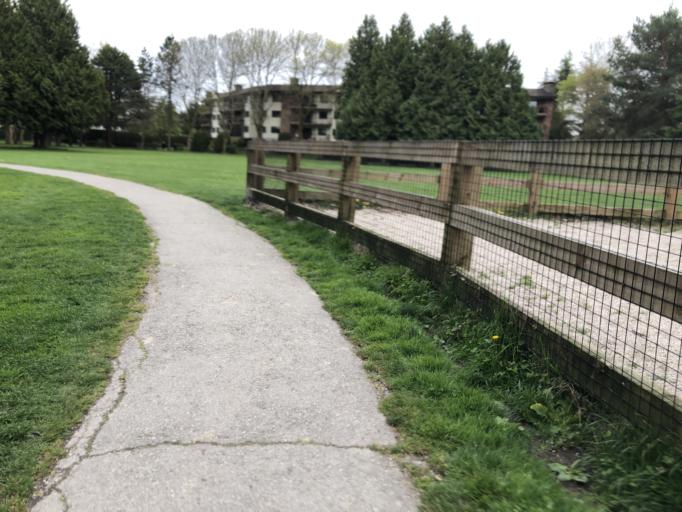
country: CA
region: British Columbia
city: Richmond
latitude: 49.1383
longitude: -123.1238
